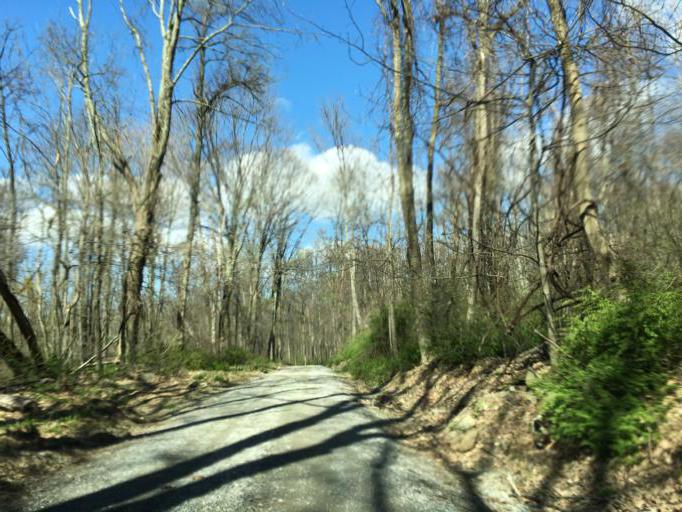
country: US
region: Maryland
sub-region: Washington County
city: Highfield-Cascade
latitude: 39.6510
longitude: -77.4793
